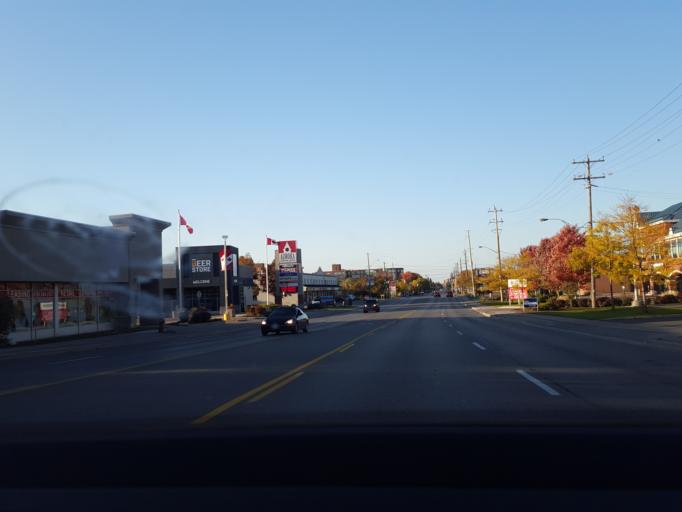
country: CA
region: Ontario
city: Newmarket
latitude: 43.9874
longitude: -79.4645
